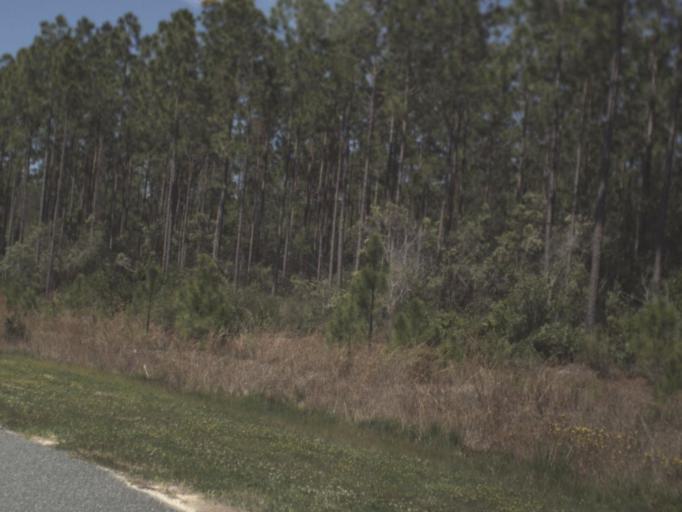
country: US
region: Florida
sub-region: Gulf County
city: Port Saint Joe
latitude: 29.8879
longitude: -85.3483
